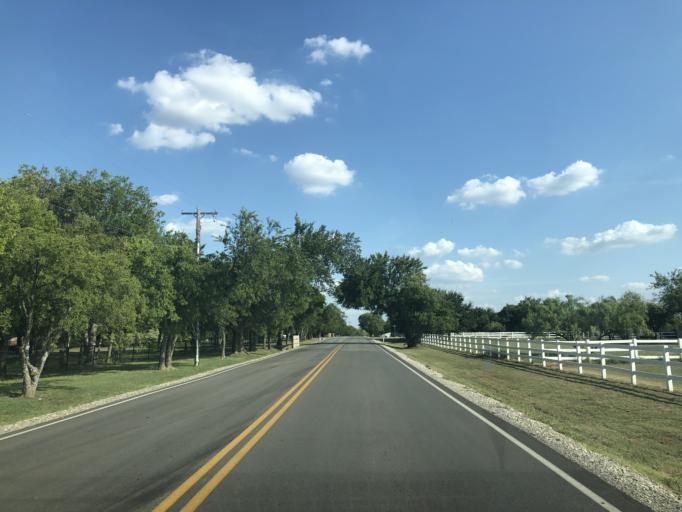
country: US
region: Texas
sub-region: Tarrant County
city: Saginaw
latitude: 32.8937
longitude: -97.3962
